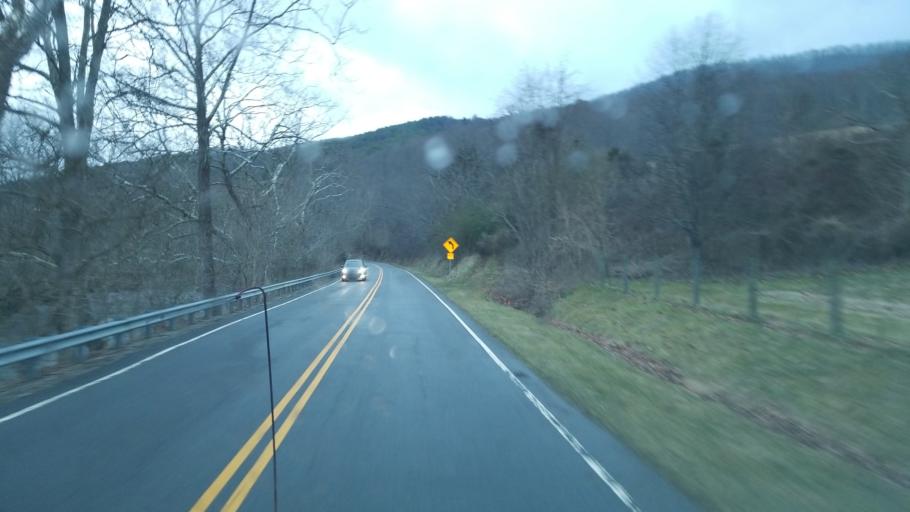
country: US
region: Virginia
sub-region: Giles County
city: Narrows
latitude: 37.1980
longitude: -80.8328
